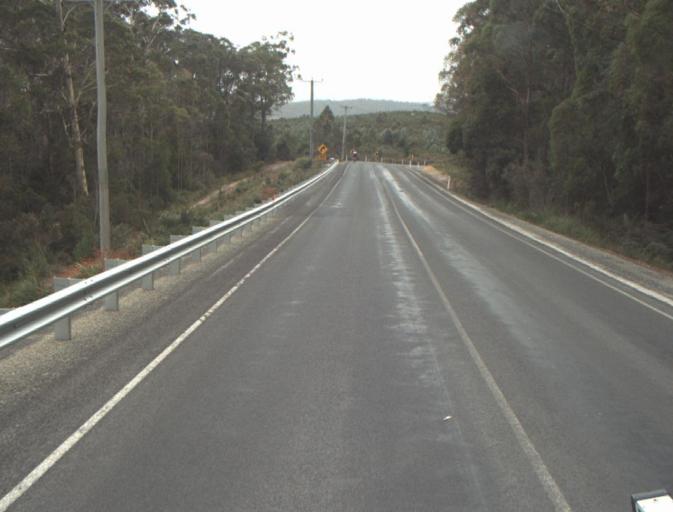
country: AU
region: Tasmania
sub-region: Dorset
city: Bridport
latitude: -41.1658
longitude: 147.2585
